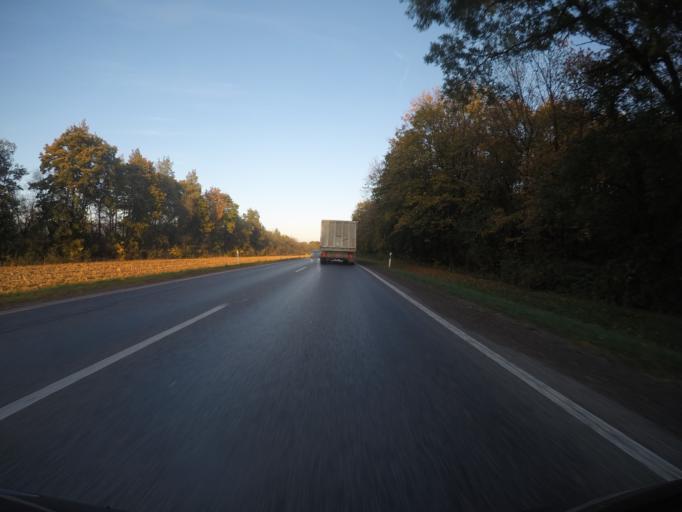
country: HU
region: Baranya
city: Pellerd
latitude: 46.0576
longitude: 18.1013
